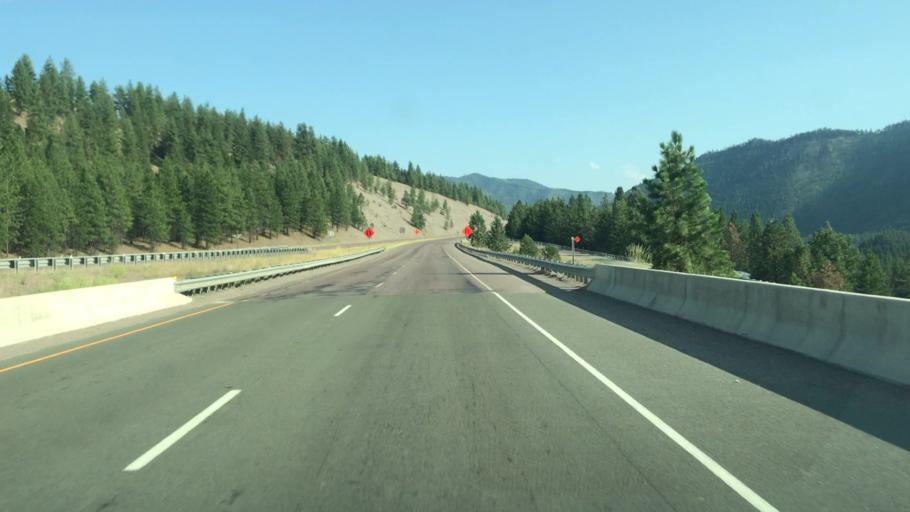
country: US
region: Montana
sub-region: Mineral County
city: Superior
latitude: 47.0259
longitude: -114.7394
